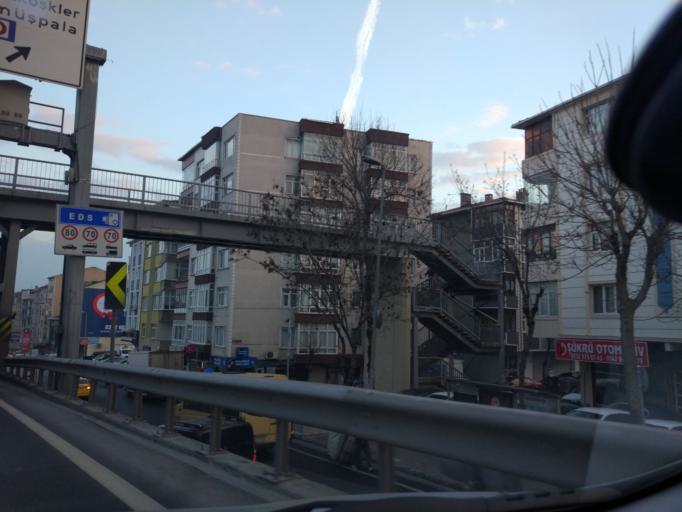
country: TR
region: Istanbul
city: Yakuplu
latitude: 40.9778
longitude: 28.7361
